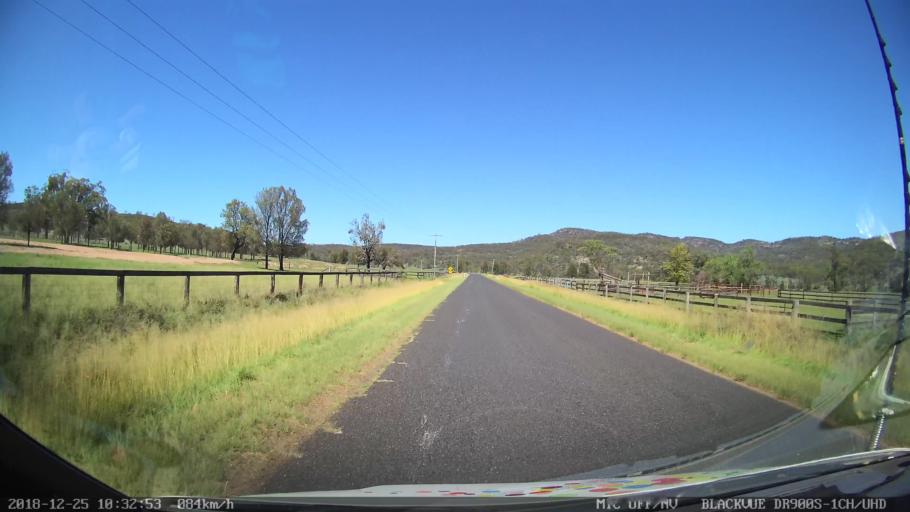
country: AU
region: New South Wales
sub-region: Upper Hunter Shire
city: Merriwa
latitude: -32.3783
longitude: 150.4128
